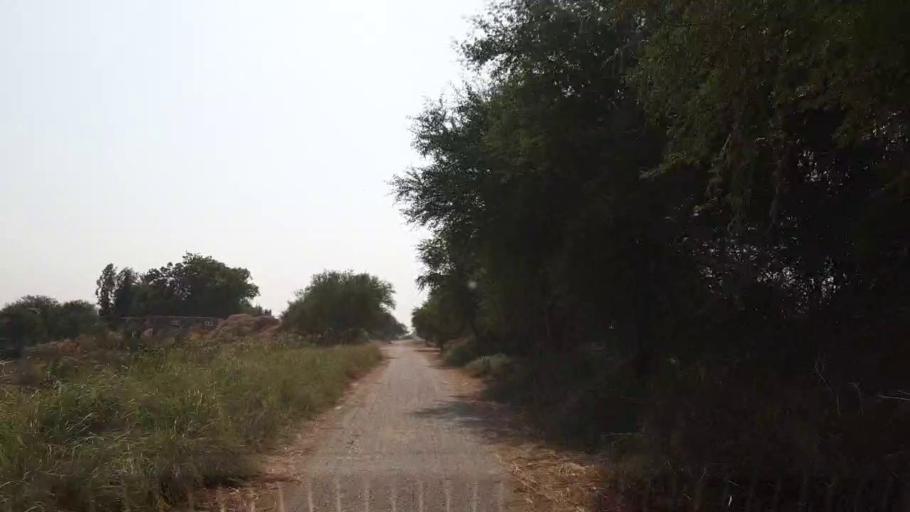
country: PK
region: Sindh
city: Bulri
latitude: 24.9570
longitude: 68.3289
